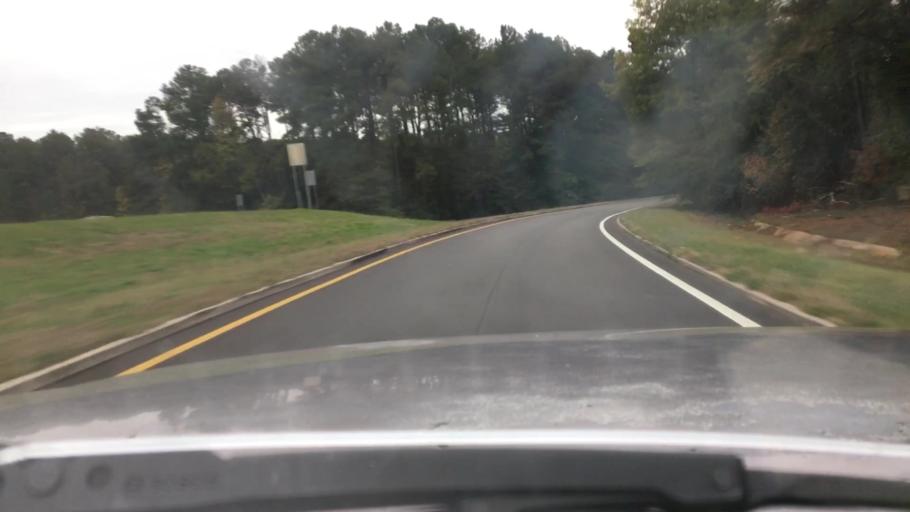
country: US
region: South Carolina
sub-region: Lexington County
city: Saint Andrews
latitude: 34.0378
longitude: -81.1136
